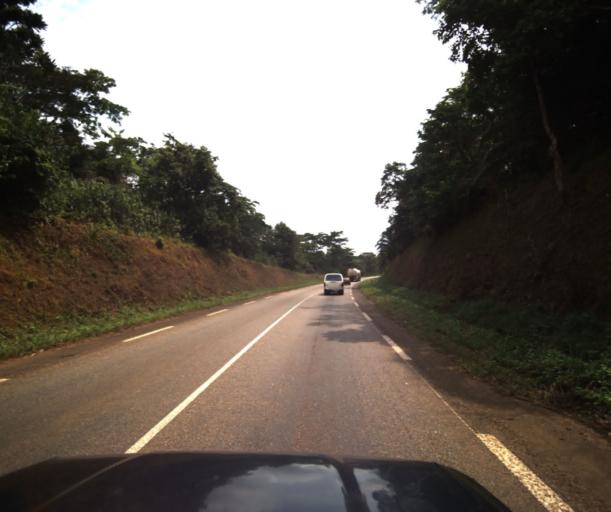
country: CM
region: Centre
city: Eseka
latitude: 3.8588
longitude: 10.5819
